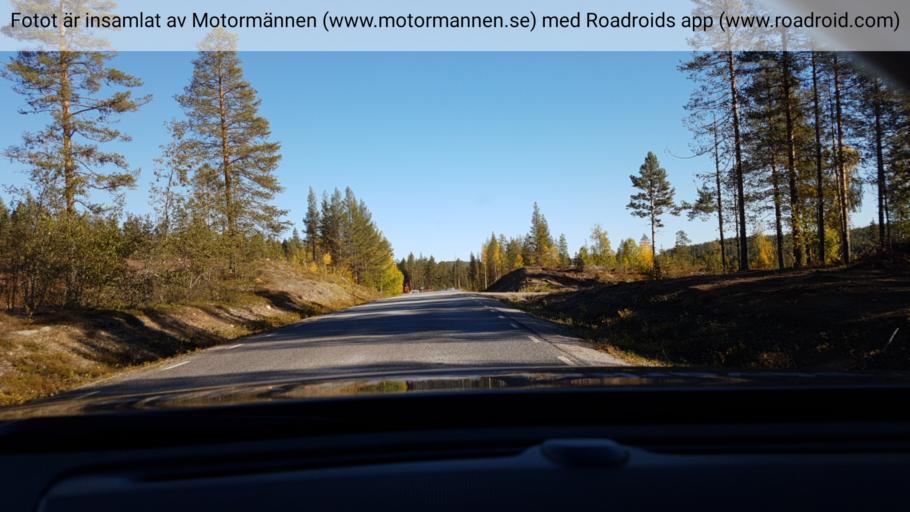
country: SE
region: Norrbotten
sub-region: Gallivare Kommun
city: Gaellivare
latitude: 66.4727
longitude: 20.8530
